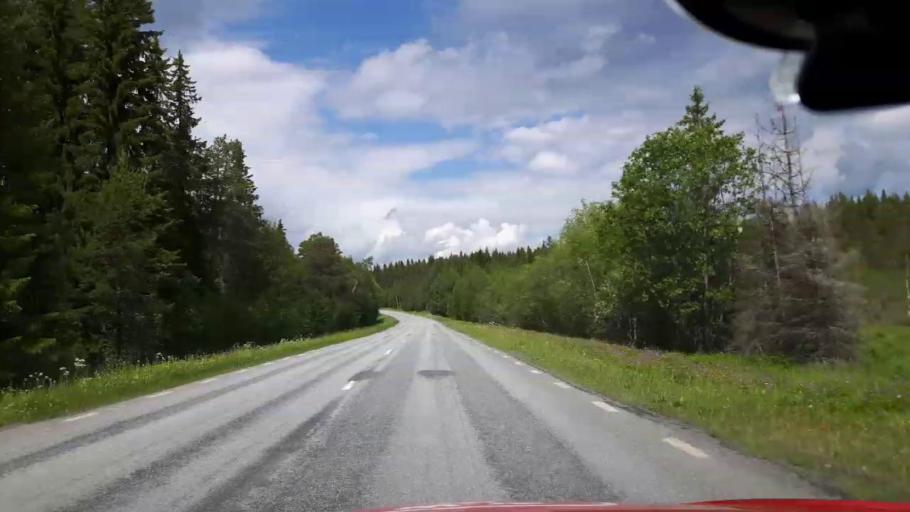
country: SE
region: Jaemtland
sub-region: Krokoms Kommun
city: Krokom
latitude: 63.3744
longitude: 14.3862
